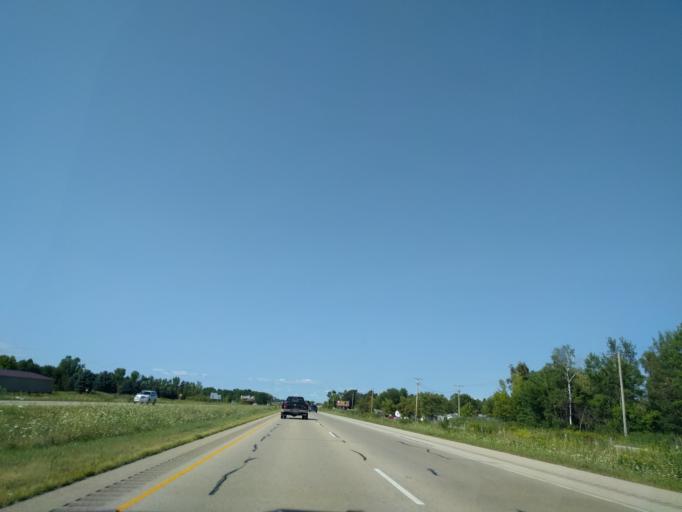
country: US
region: Wisconsin
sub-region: Brown County
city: Suamico
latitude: 44.6942
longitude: -88.0506
